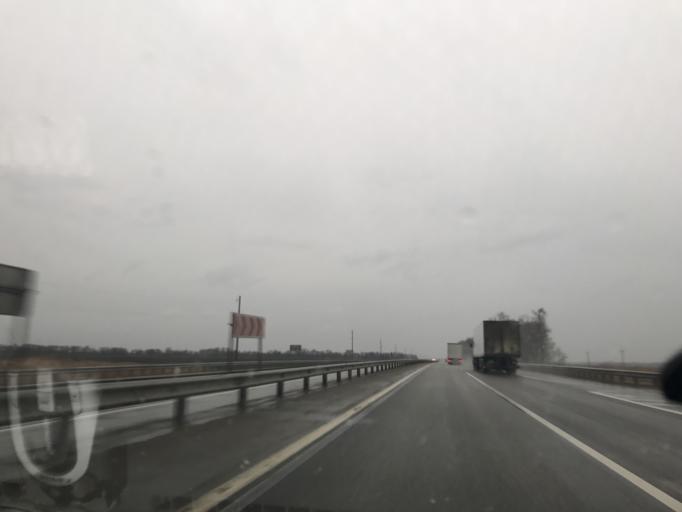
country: RU
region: Krasnodarskiy
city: Kislyakovskaya
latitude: 46.3892
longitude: 39.7387
